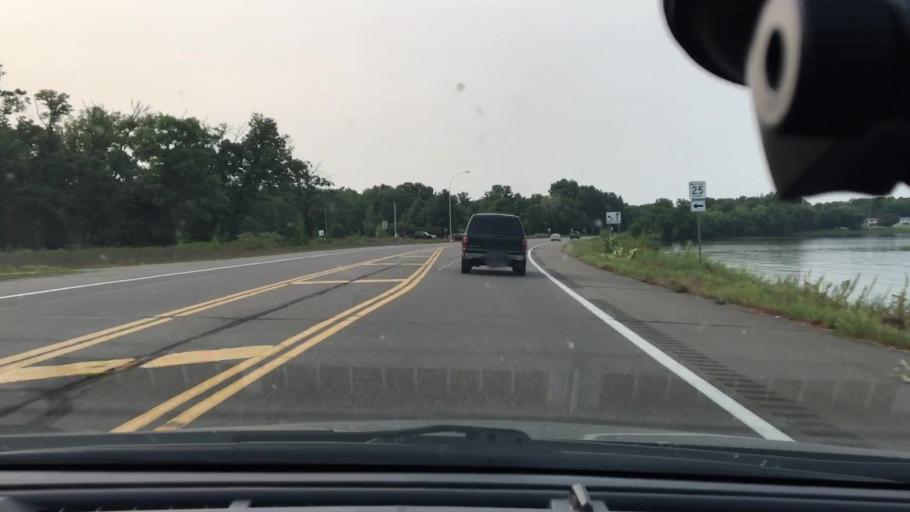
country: US
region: Minnesota
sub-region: Mille Lacs County
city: Vineland
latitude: 46.2131
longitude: -93.7924
